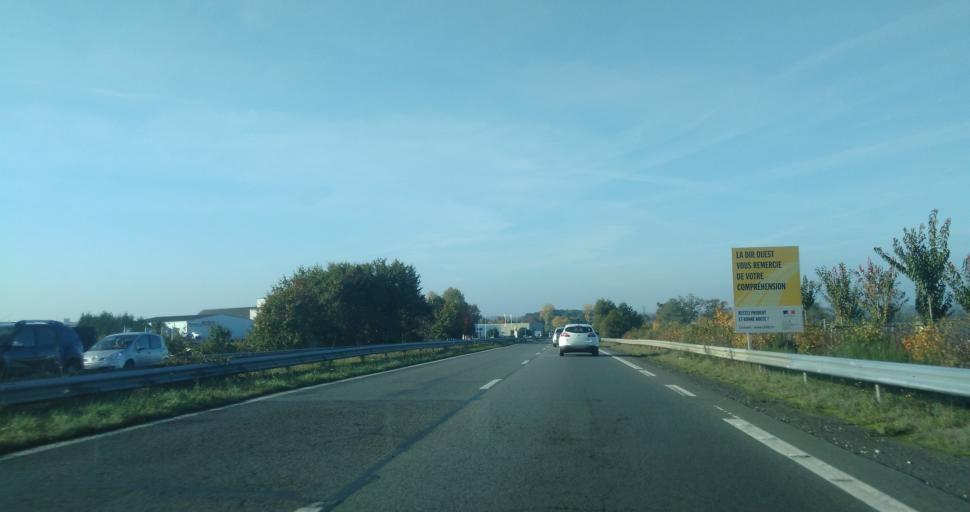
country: FR
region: Brittany
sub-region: Departement d'Ille-et-Vilaine
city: Breal-sous-Montfort
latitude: 48.0618
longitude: -1.8743
